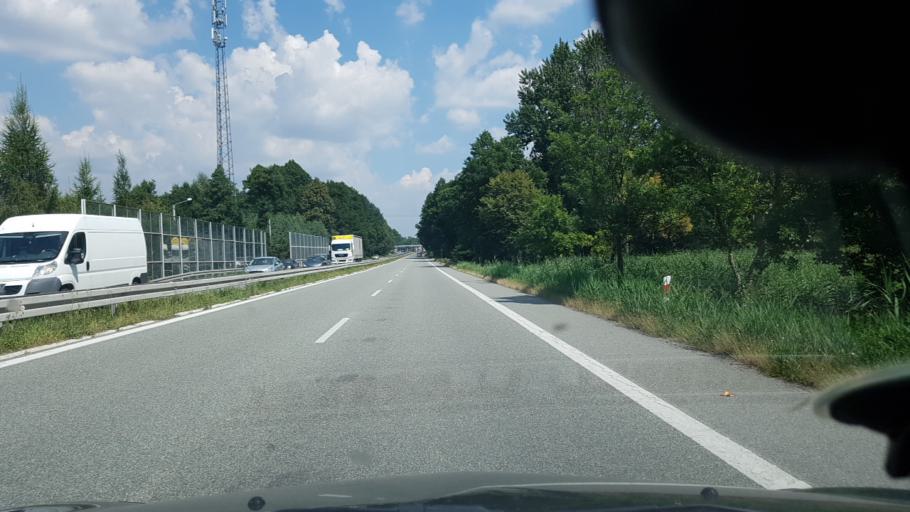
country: PL
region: Silesian Voivodeship
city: Gardawice
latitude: 50.1164
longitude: 18.8062
